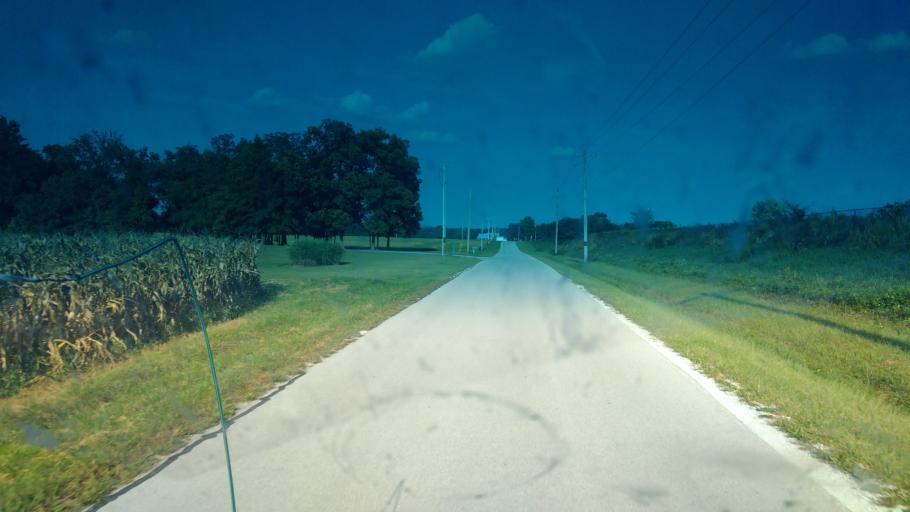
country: US
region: Ohio
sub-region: Wyandot County
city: Carey
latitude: 40.9215
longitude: -83.3249
